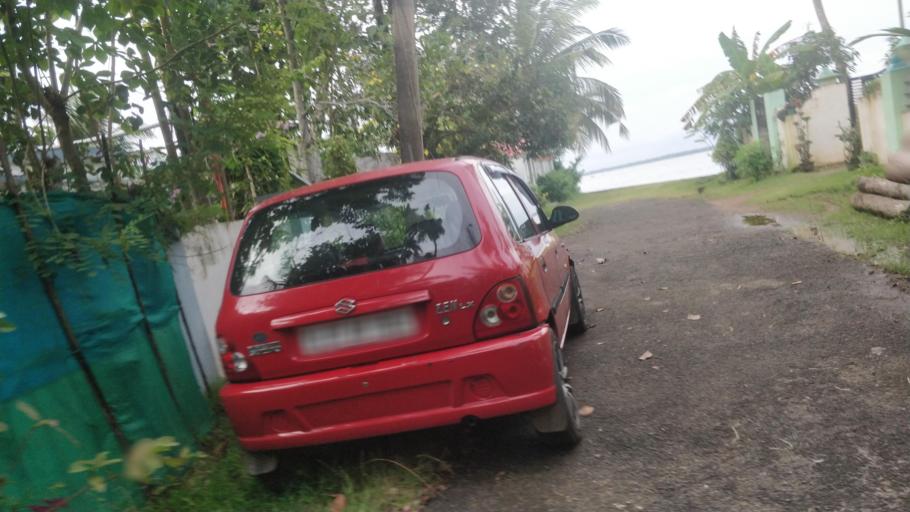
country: IN
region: Kerala
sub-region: Alappuzha
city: Shertallai
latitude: 9.6976
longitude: 76.3629
